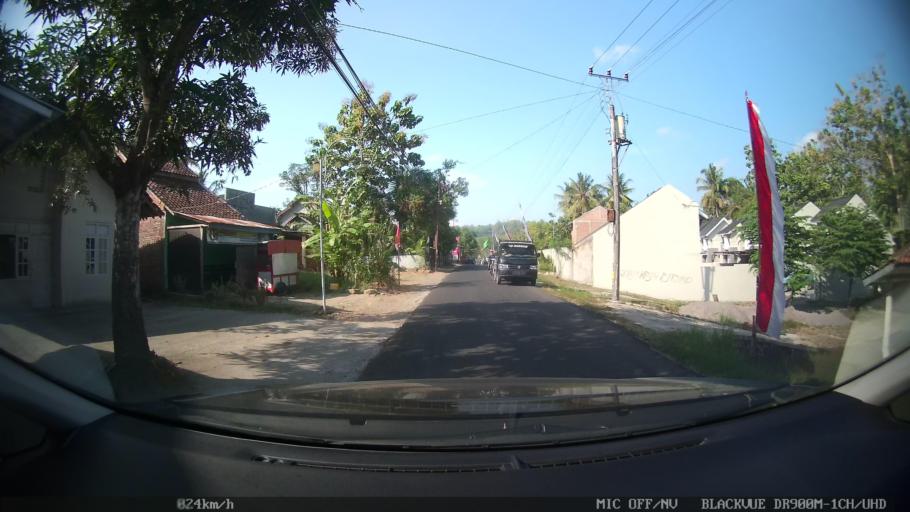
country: ID
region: Daerah Istimewa Yogyakarta
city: Godean
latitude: -7.8212
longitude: 110.2740
